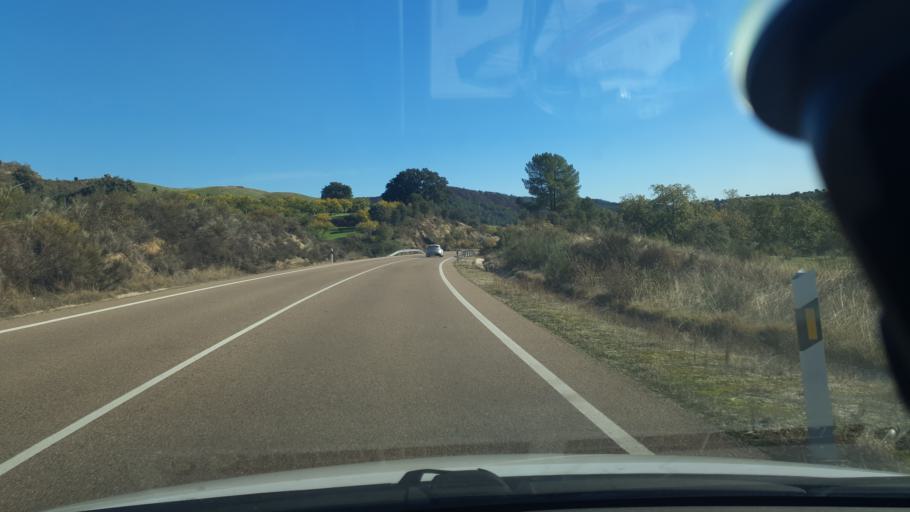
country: ES
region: Castille and Leon
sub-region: Provincia de Avila
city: Poyales del Hoyo
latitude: 40.1589
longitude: -5.1624
